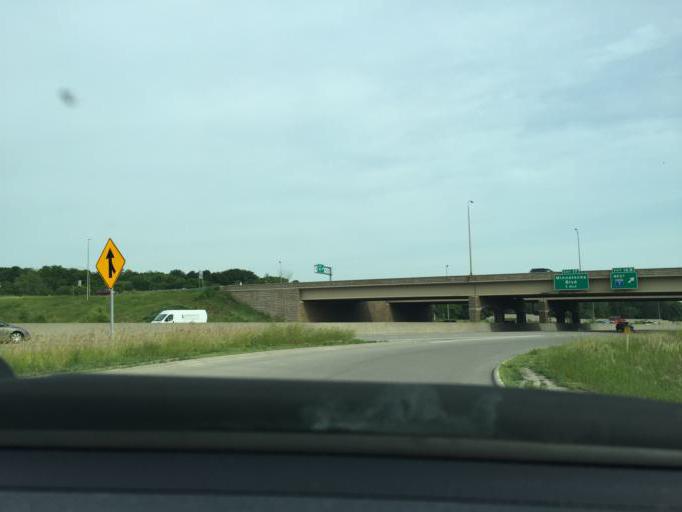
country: US
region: Minnesota
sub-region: Hennepin County
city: Hopkins
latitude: 44.9241
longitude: -93.4510
